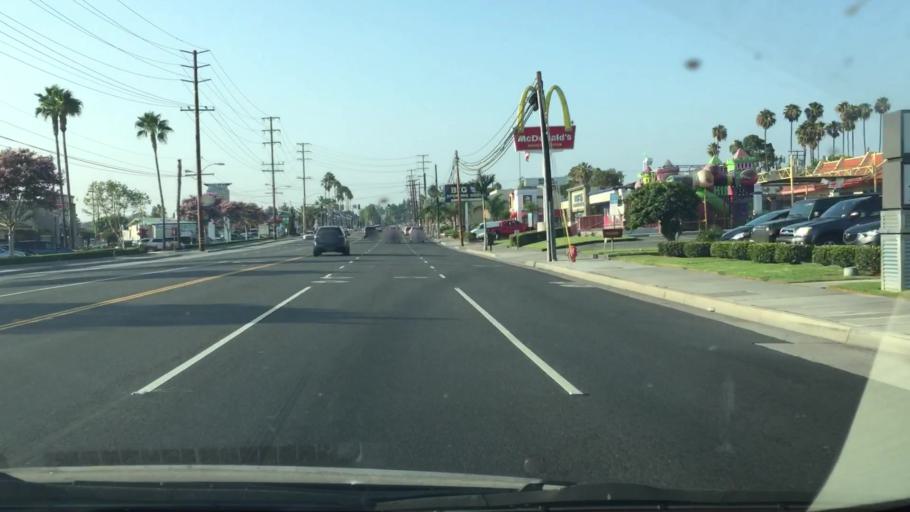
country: US
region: California
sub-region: Orange County
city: Villa Park
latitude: 33.8282
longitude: -117.8361
